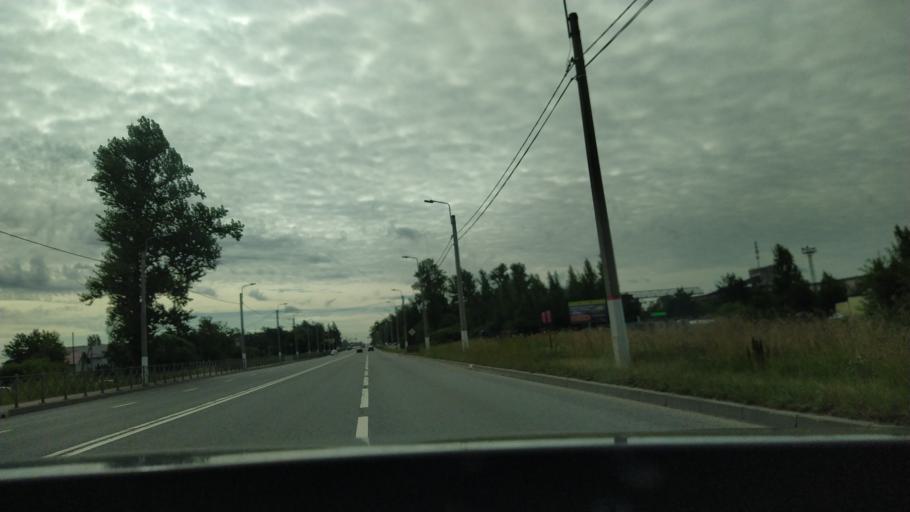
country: RU
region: Leningrad
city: Tosno
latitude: 59.5620
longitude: 30.8386
